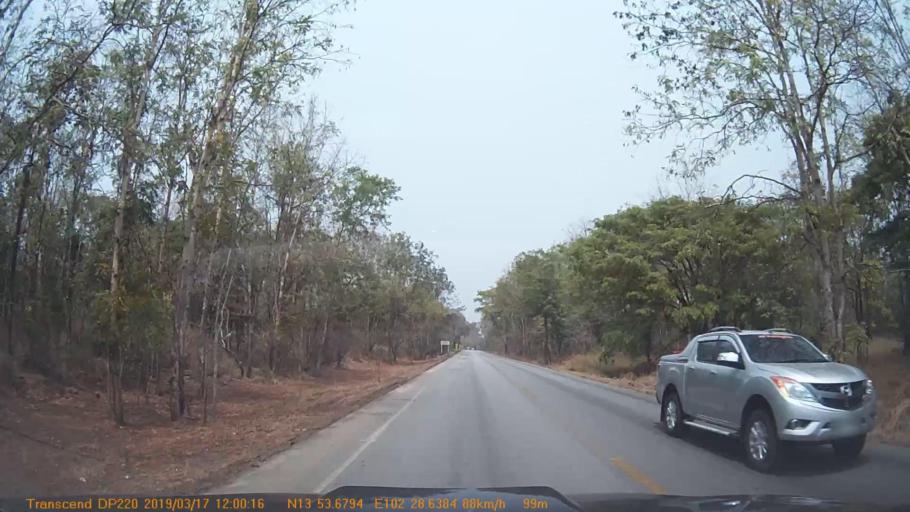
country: TH
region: Sa Kaeo
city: Khok Sung
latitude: 13.8950
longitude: 102.4771
